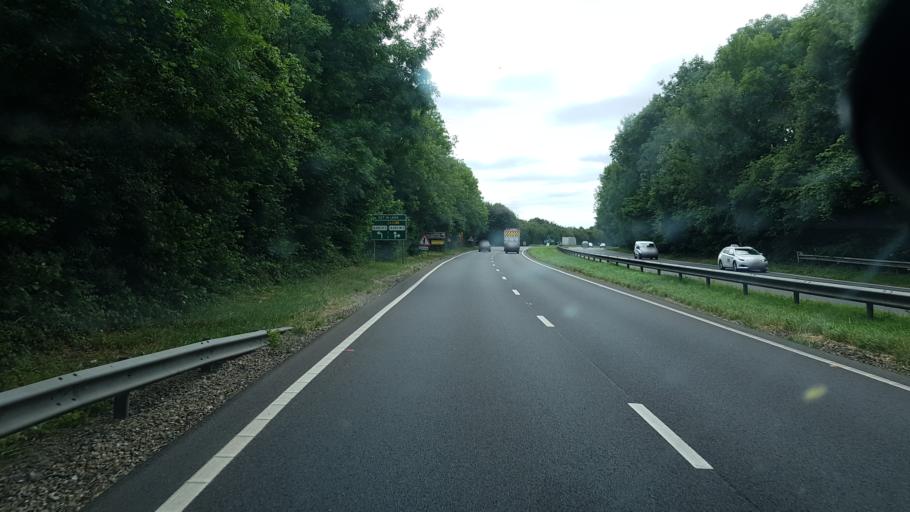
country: GB
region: England
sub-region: Surrey
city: Godstone
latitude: 51.2538
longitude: -0.0556
